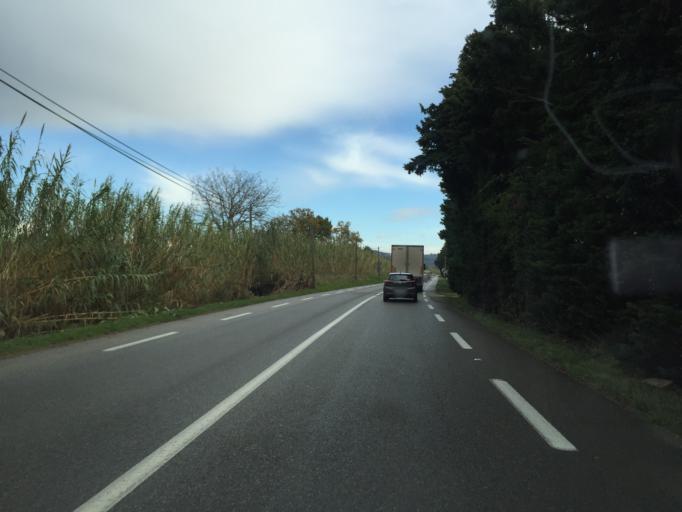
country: FR
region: Provence-Alpes-Cote d'Azur
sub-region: Departement du Vaucluse
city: Lagnes
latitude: 43.8749
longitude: 5.0878
